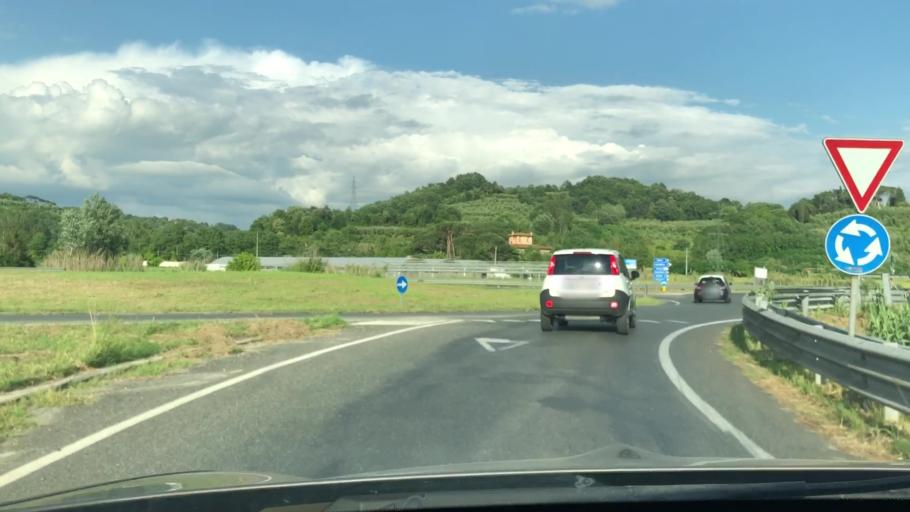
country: IT
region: Tuscany
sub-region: Province of Pisa
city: Treggiaia
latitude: 43.6185
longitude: 10.6740
